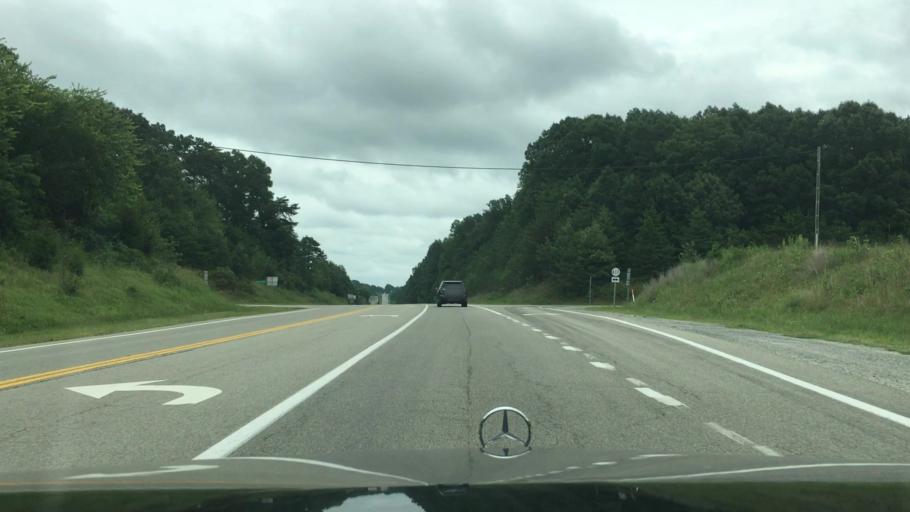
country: US
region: Virginia
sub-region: Nottoway County
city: Crewe
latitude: 37.2749
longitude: -78.2360
